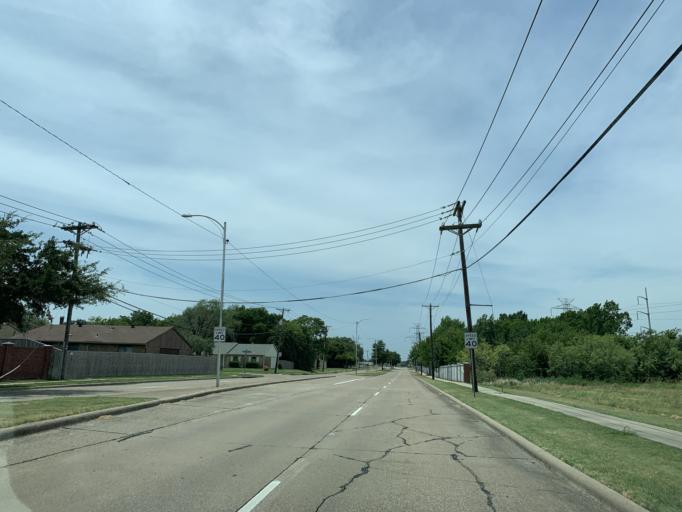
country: US
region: Texas
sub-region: Dallas County
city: Grand Prairie
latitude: 32.6584
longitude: -97.0169
